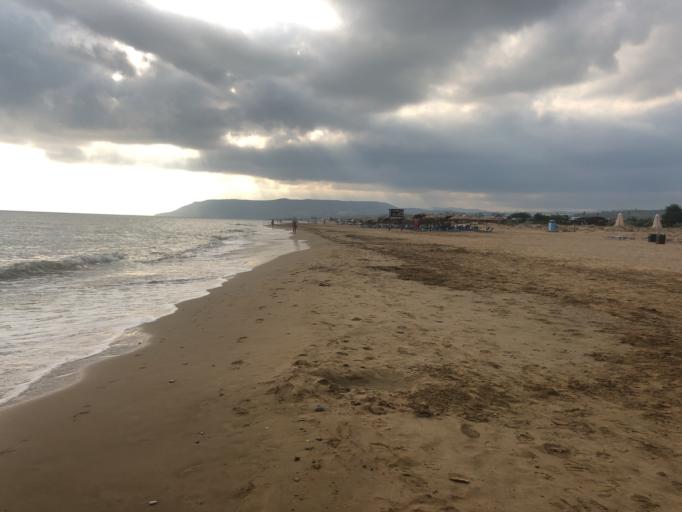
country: GR
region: Crete
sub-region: Nomos Chanias
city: Georgioupolis
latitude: 35.3556
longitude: 24.2860
